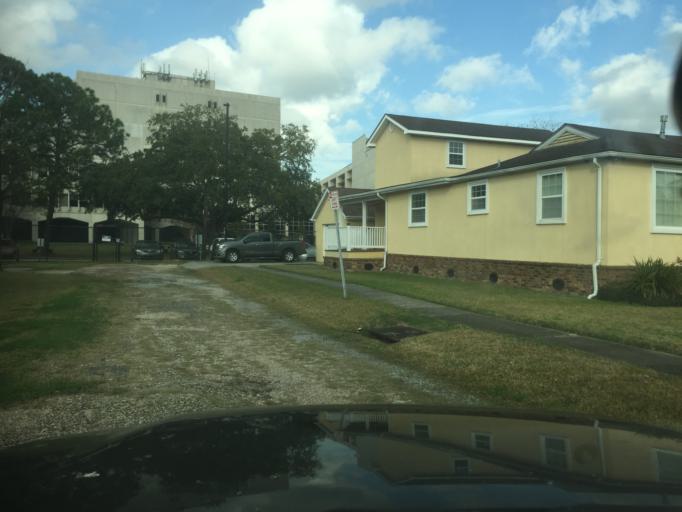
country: US
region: Louisiana
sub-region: Orleans Parish
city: New Orleans
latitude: 29.9900
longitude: -90.0841
